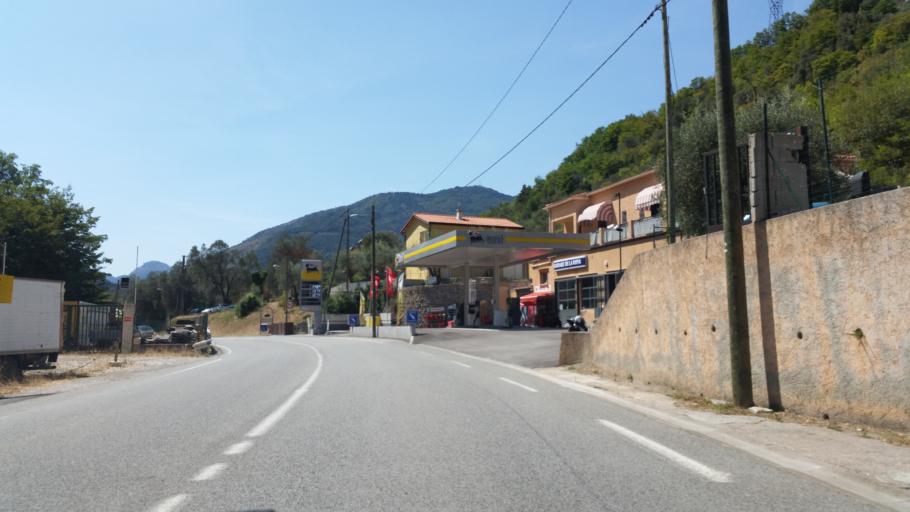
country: FR
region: Provence-Alpes-Cote d'Azur
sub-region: Departement des Alpes-Maritimes
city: Breil-sur-Roya
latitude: 43.9581
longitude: 7.5210
